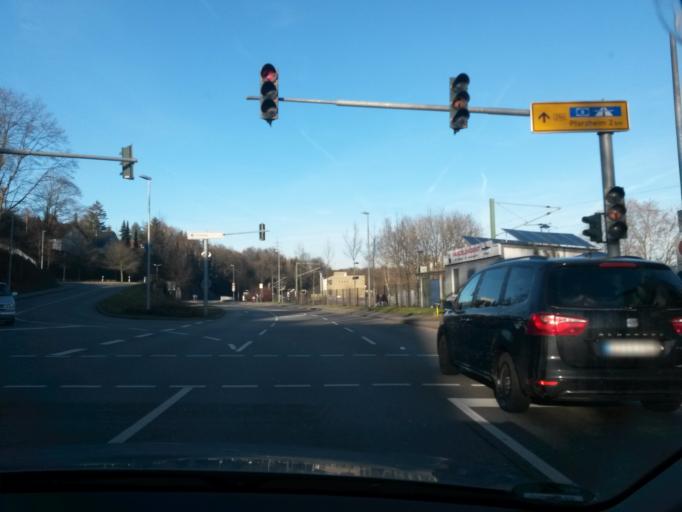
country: DE
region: Baden-Wuerttemberg
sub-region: Karlsruhe Region
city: Birkenfeld
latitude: 48.8734
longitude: 8.6450
